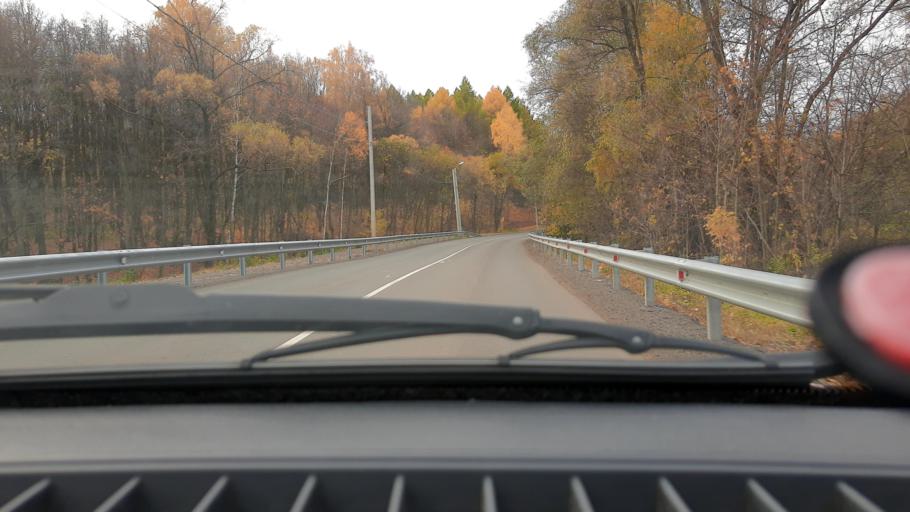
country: RU
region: Bashkortostan
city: Avdon
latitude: 54.6651
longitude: 55.7100
